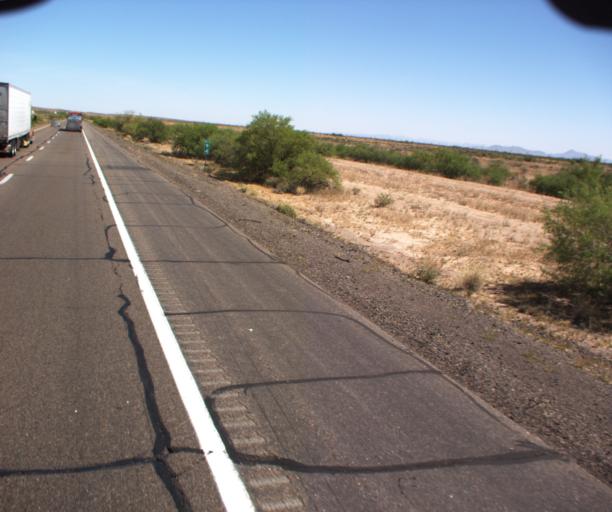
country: US
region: Arizona
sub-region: Maricopa County
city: Gila Bend
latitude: 32.8820
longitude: -113.0978
